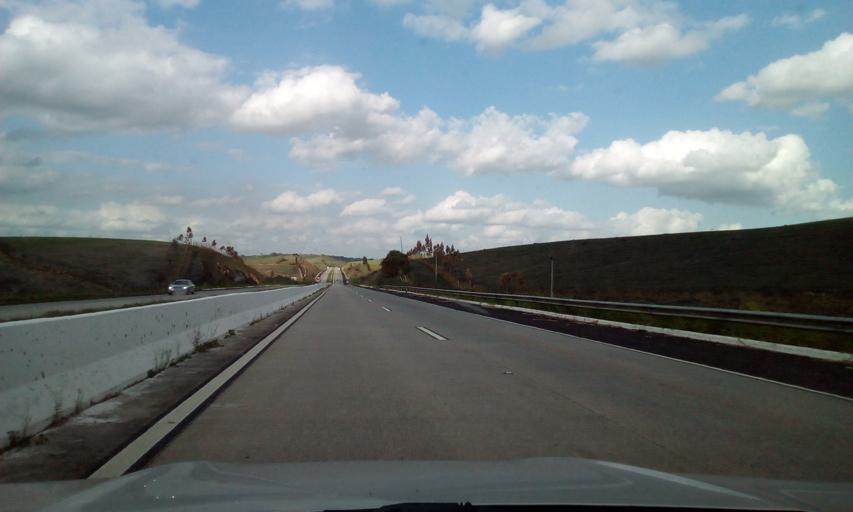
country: BR
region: Pernambuco
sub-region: Gameleira
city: Gameleira
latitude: -8.5635
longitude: -35.4709
